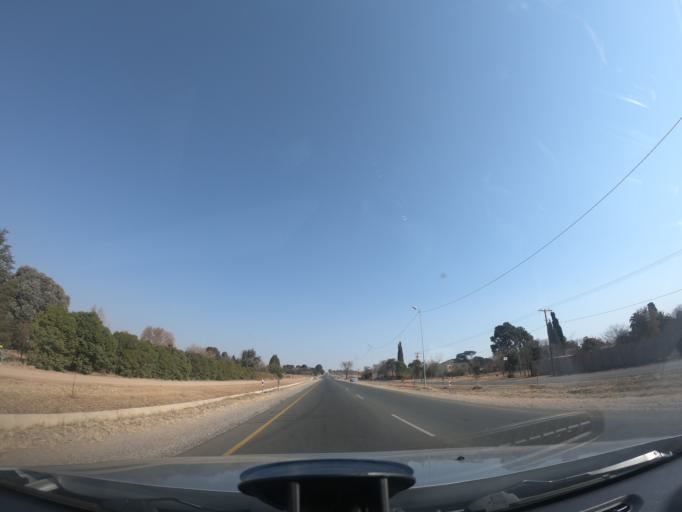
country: ZA
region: Gauteng
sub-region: City of Johannesburg Metropolitan Municipality
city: Diepsloot
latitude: -25.8527
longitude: 28.0378
